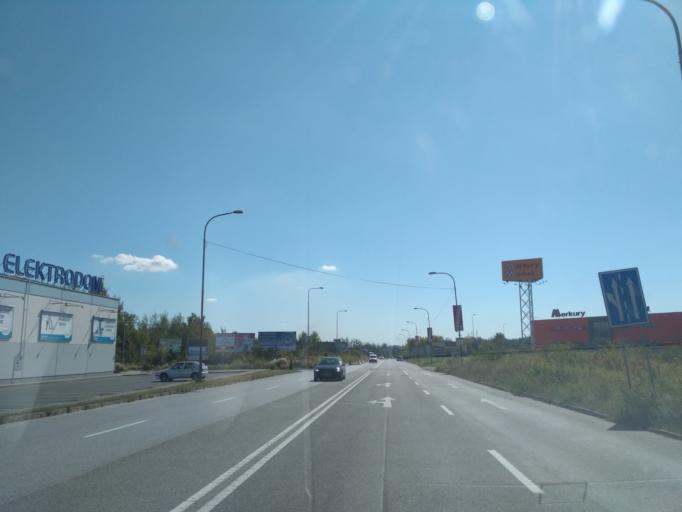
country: SK
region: Kosicky
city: Kosice
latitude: 48.6961
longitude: 21.2466
